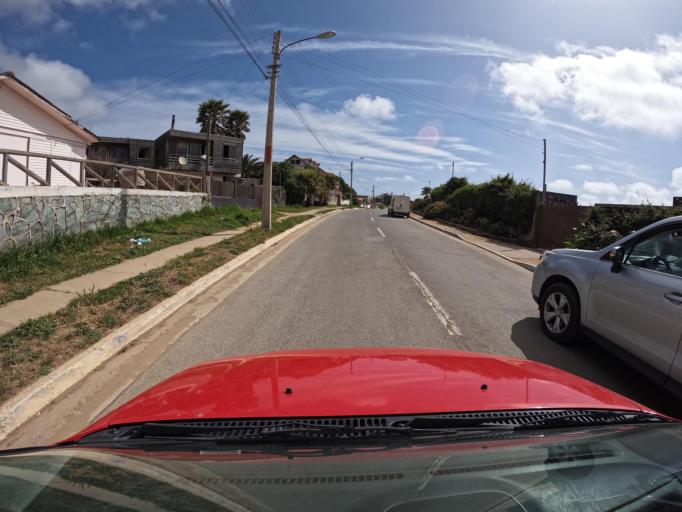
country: CL
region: O'Higgins
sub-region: Provincia de Colchagua
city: Santa Cruz
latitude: -34.3891
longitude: -72.0190
